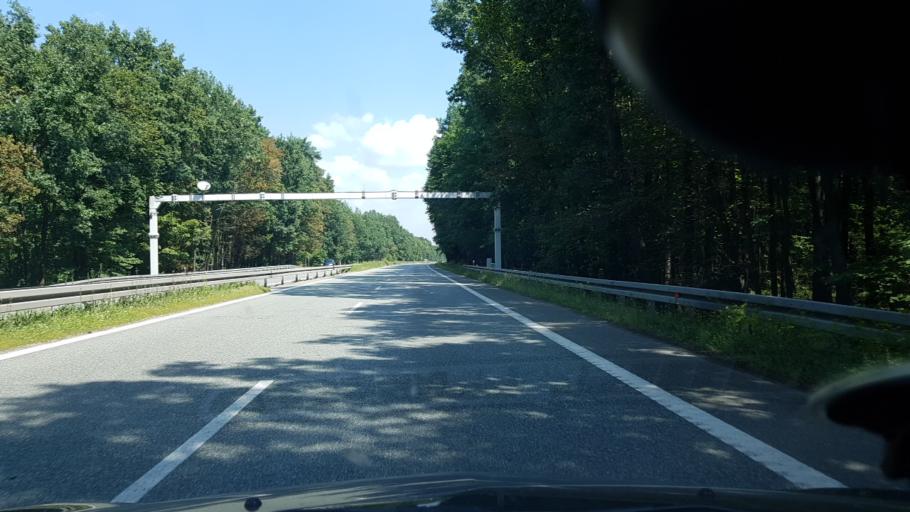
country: PL
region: Silesian Voivodeship
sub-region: Zory
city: Zory
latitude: 50.0651
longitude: 18.7277
